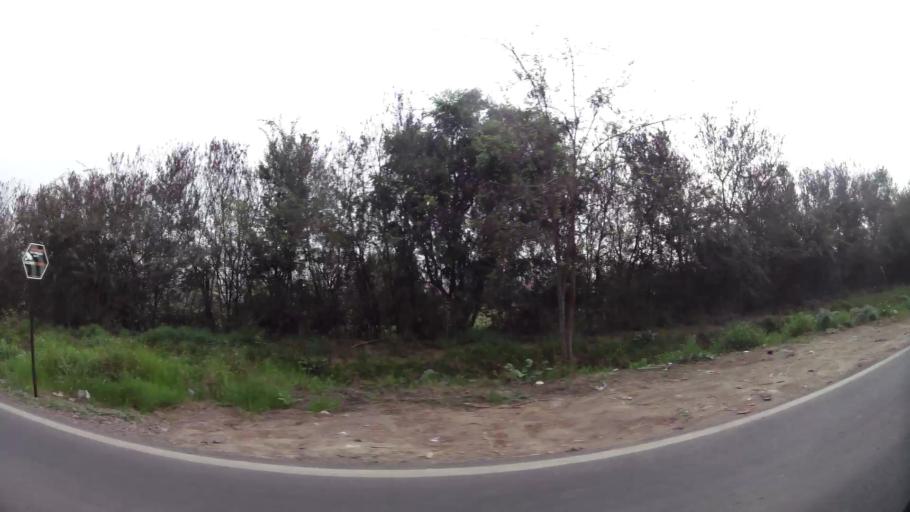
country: CL
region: Santiago Metropolitan
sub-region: Provincia de Chacabuco
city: Chicureo Abajo
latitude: -33.2707
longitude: -70.7097
